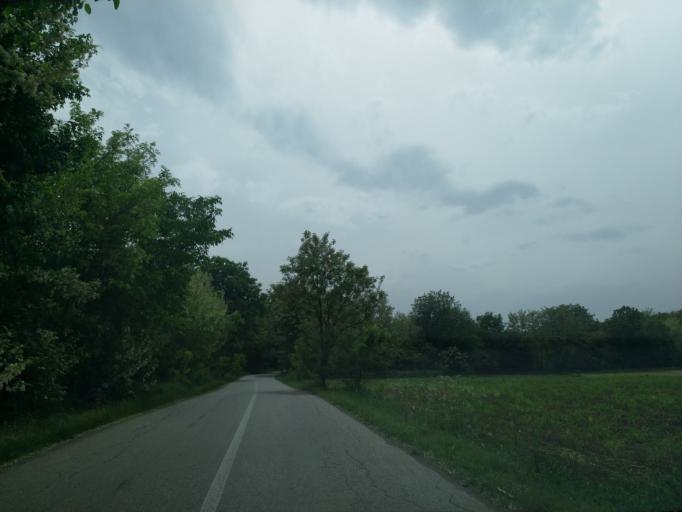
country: RS
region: Central Serbia
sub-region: Pomoravski Okrug
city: Paracin
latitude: 43.8673
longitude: 21.5389
